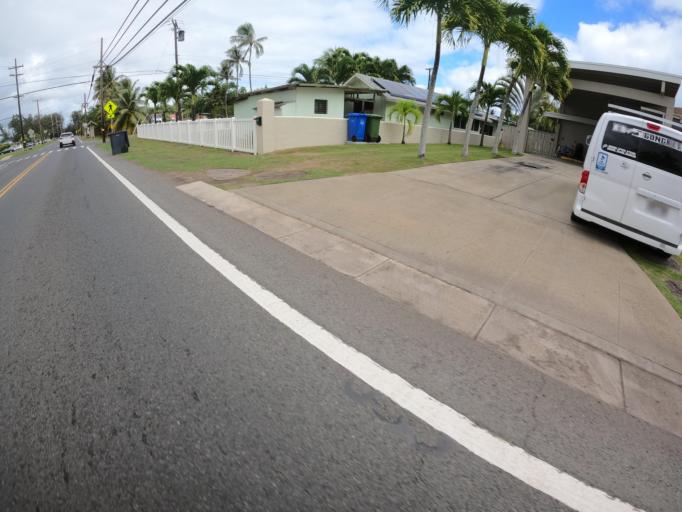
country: US
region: Hawaii
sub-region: Honolulu County
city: Waimanalo Beach
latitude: 21.3381
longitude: -157.7021
